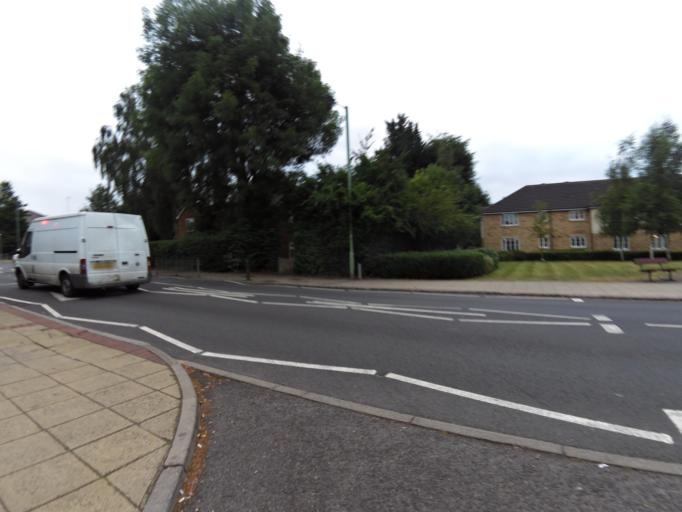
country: GB
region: England
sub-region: Hertfordshire
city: Shenley AV
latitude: 51.7243
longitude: -0.2959
